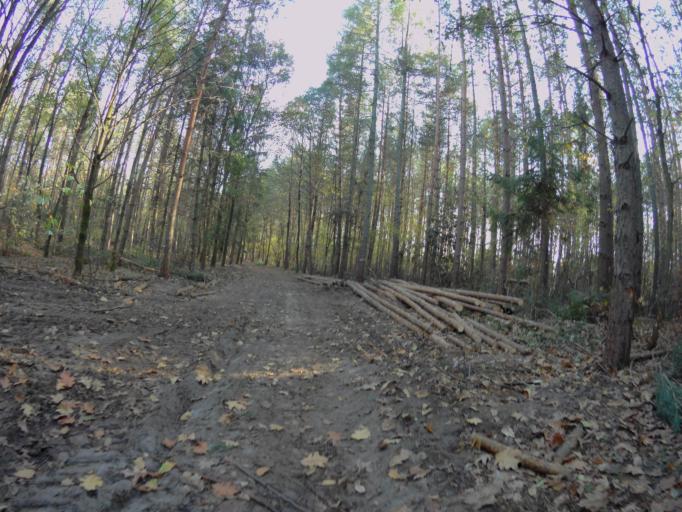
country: PL
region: Subcarpathian Voivodeship
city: Nowa Sarzyna
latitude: 50.3060
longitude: 22.3539
